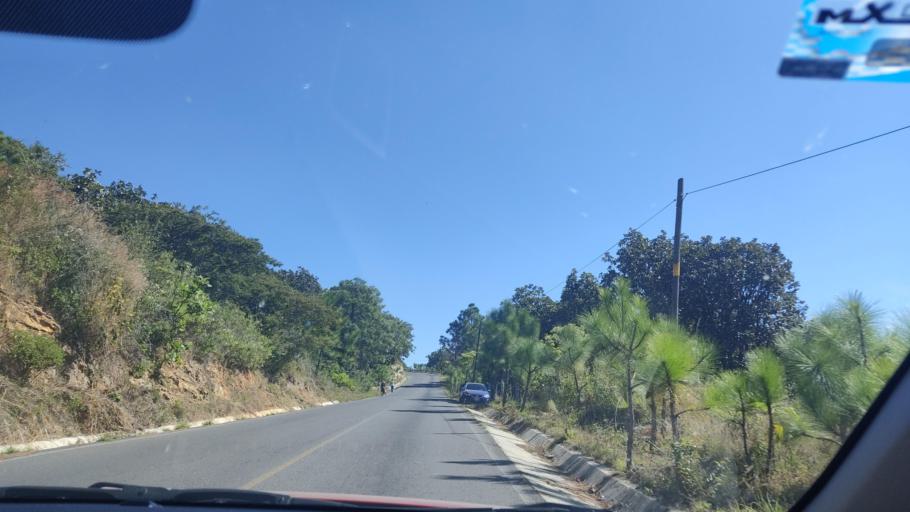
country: MX
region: Nayarit
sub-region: Jala
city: Rosa Blanca
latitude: 21.0993
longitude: -104.3649
